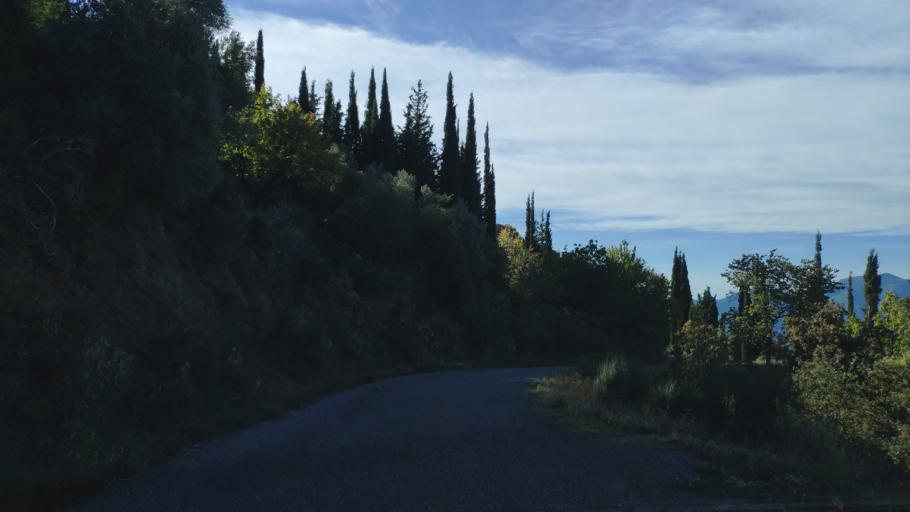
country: GR
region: Peloponnese
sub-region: Nomos Arkadias
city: Dimitsana
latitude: 37.5550
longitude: 22.0600
